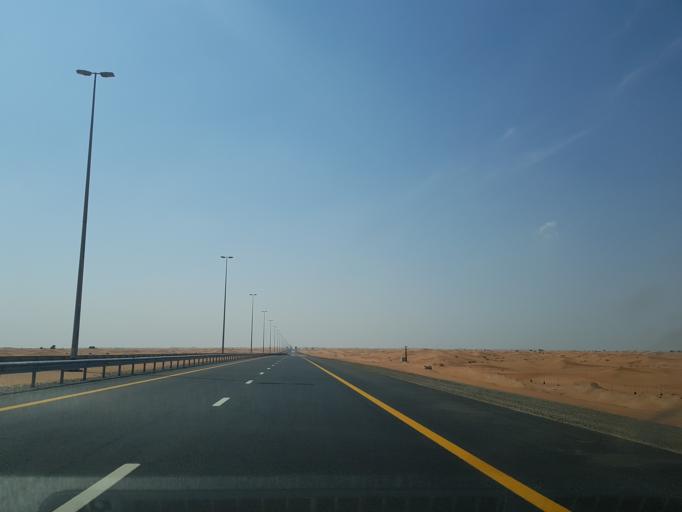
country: AE
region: Ash Shariqah
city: Adh Dhayd
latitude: 25.2538
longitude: 55.7575
